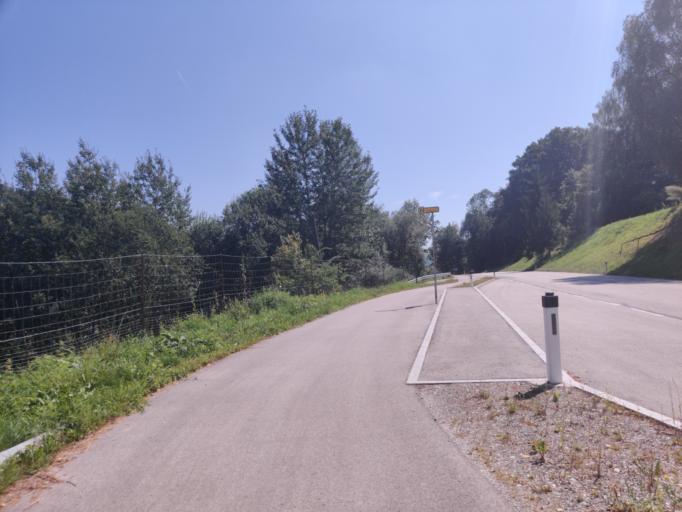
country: AT
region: Upper Austria
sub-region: Politischer Bezirk Rohrbach
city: Pfarrkirchen im Muehlkreis
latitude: 48.4825
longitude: 13.7555
